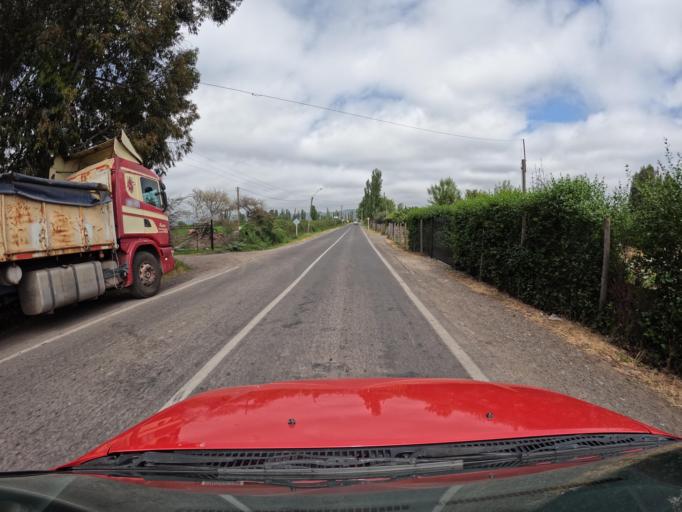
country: CL
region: O'Higgins
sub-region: Provincia de Colchagua
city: Santa Cruz
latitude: -34.6769
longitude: -71.3563
